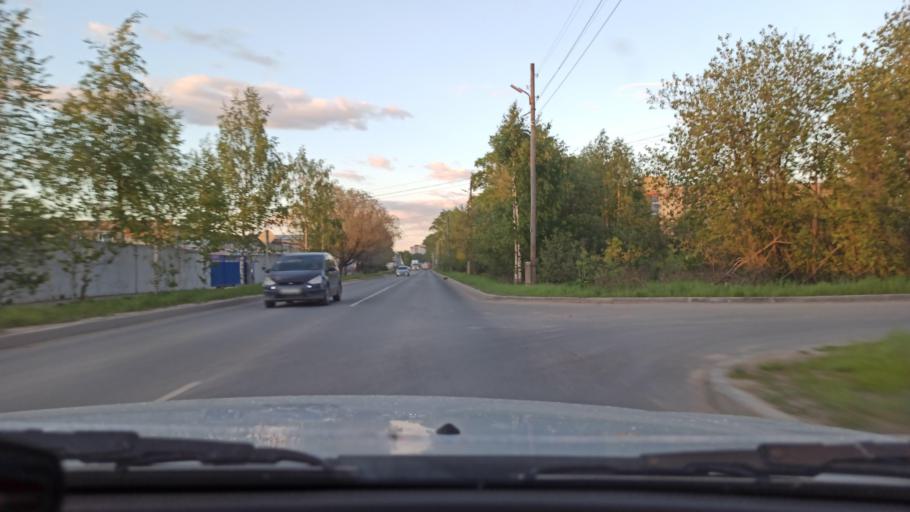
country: RU
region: Vologda
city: Vologda
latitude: 59.2205
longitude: 39.8385
